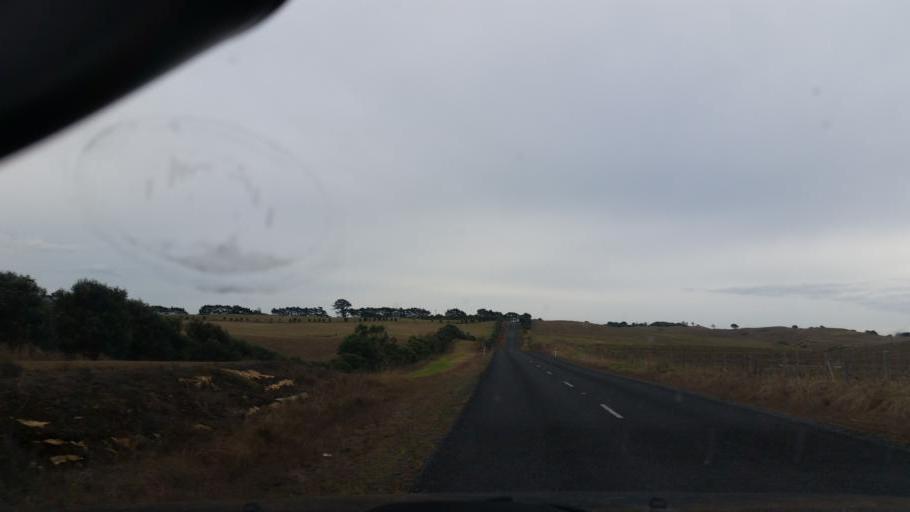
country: NZ
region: Northland
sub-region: Kaipara District
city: Dargaville
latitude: -36.0447
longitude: 173.8778
